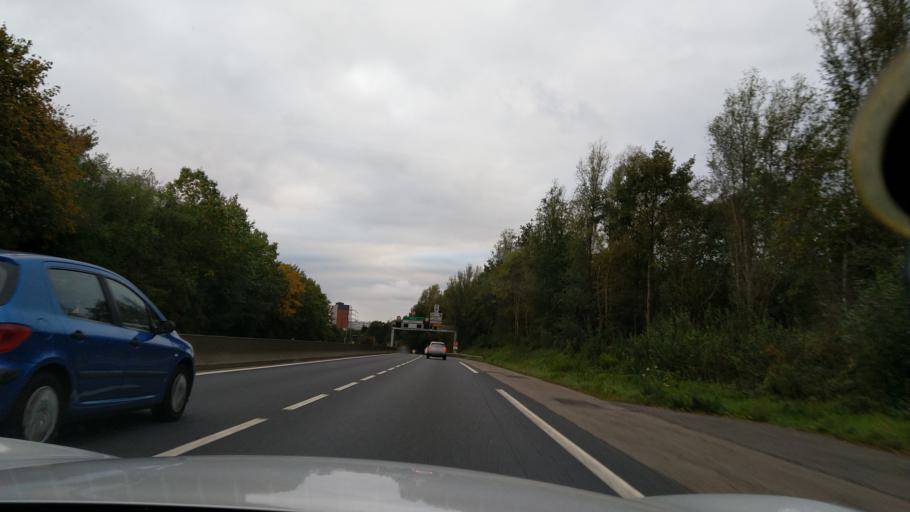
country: FR
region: Haute-Normandie
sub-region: Departement de la Seine-Maritime
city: Bois-Guillaume
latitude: 49.4713
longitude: 1.1340
